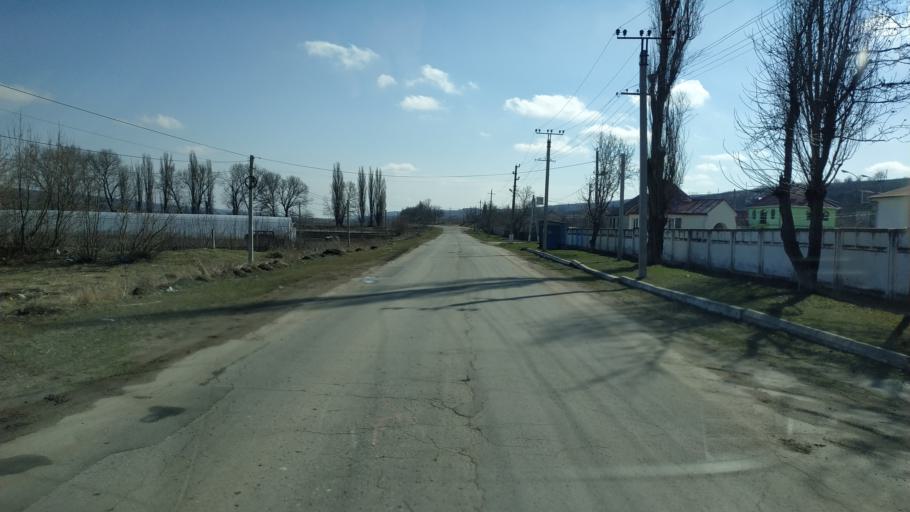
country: MD
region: Hincesti
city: Hincesti
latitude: 46.9531
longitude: 28.6095
